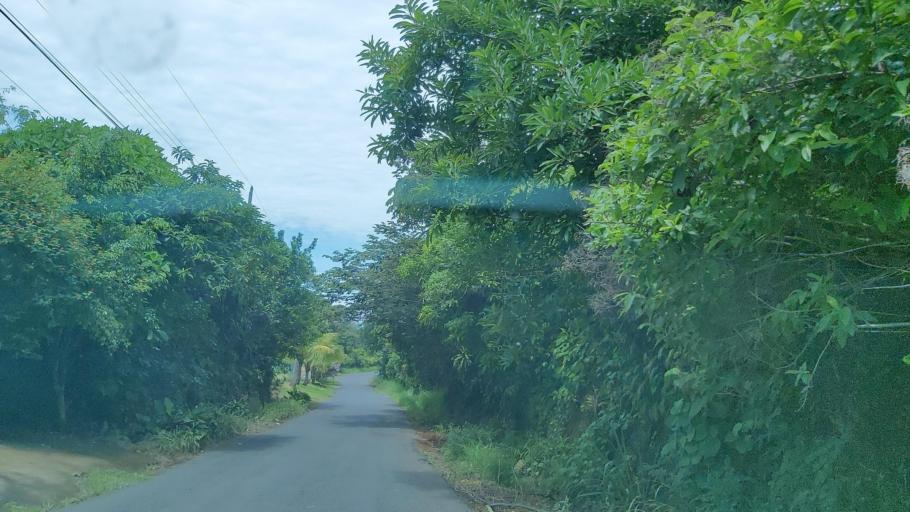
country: CR
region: Alajuela
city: San Juan
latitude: 10.1033
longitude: -84.3347
